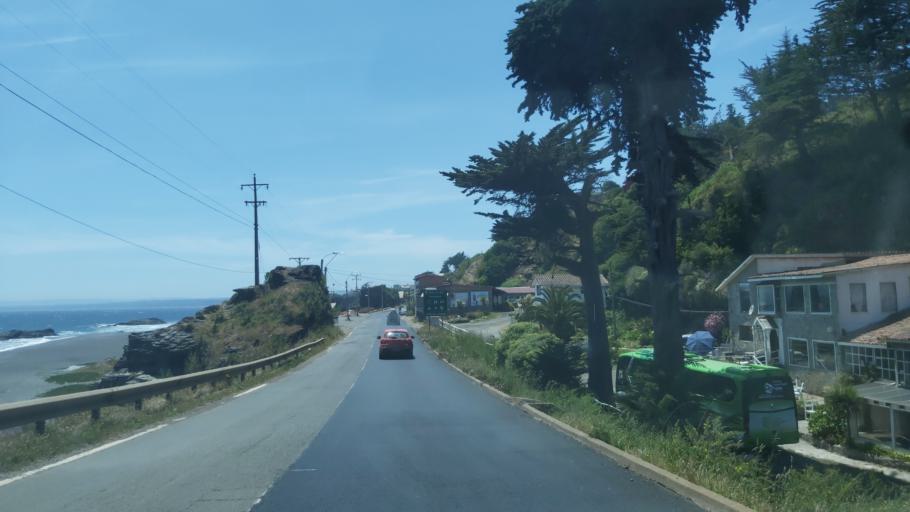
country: CL
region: Maule
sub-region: Provincia de Cauquenes
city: Cauquenes
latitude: -35.8227
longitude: -72.6006
